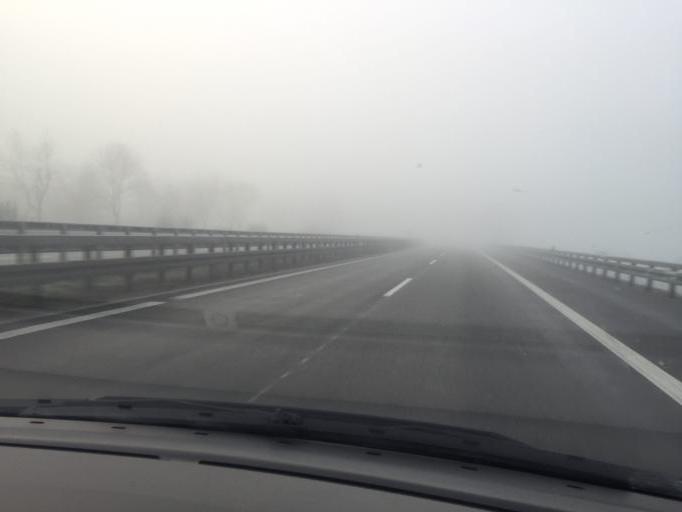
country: DE
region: Baden-Wuerttemberg
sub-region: Freiburg Region
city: Donaueschingen
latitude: 47.9749
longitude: 8.5141
